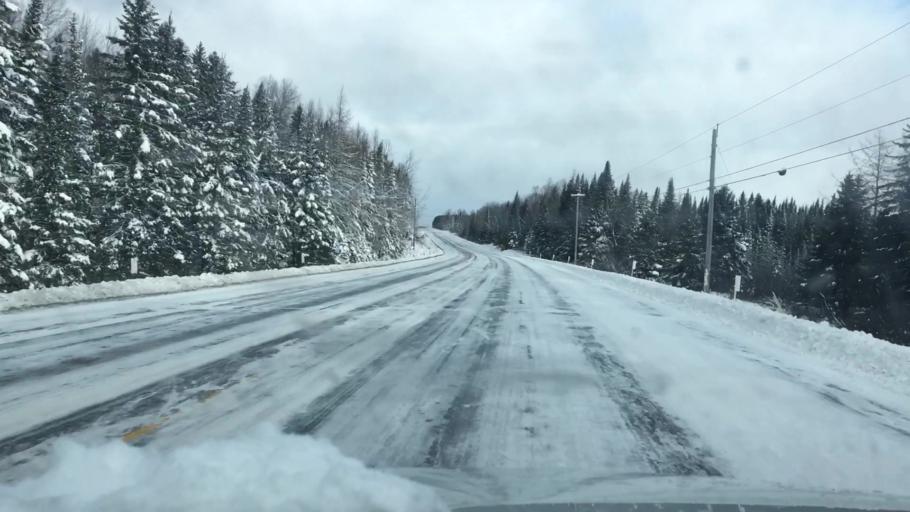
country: US
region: Maine
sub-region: Aroostook County
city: Van Buren
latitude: 47.0713
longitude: -67.9864
